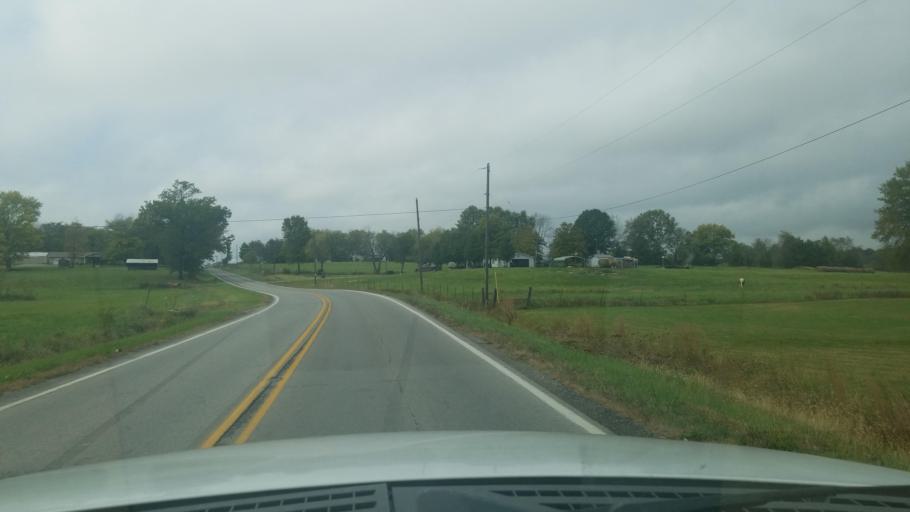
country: US
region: Illinois
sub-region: Saline County
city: Harrisburg
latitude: 37.8412
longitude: -88.6187
